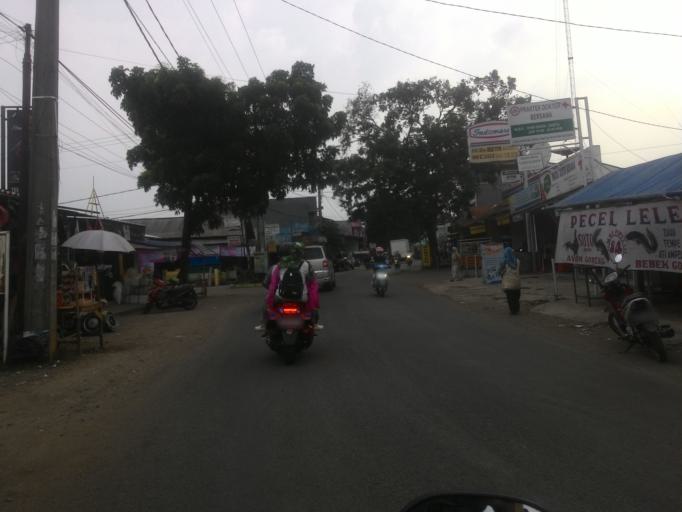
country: ID
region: West Java
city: Cibinong
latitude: -6.4628
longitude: 106.8247
